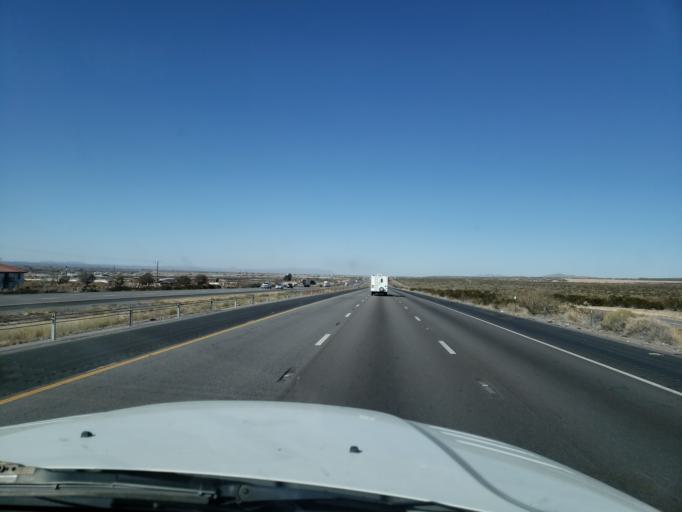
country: US
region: New Mexico
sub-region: Dona Ana County
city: Mesquite
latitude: 32.1585
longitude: -106.6586
